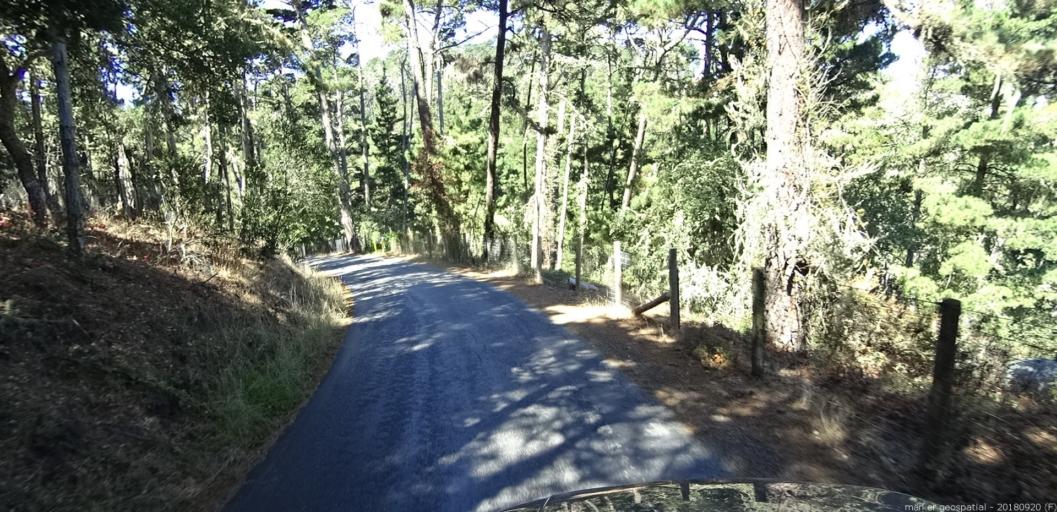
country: US
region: California
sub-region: Monterey County
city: Monterey
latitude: 36.5735
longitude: -121.9008
